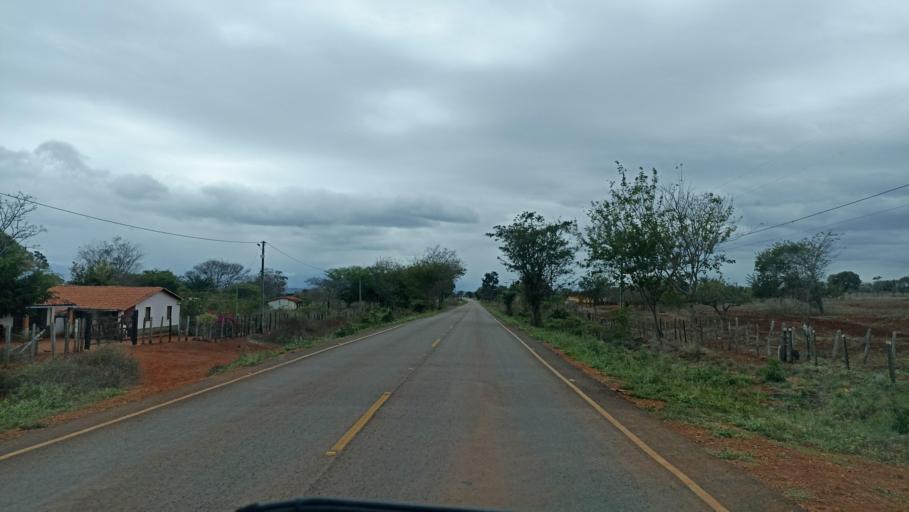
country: BR
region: Bahia
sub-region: Andarai
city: Vera Cruz
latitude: -12.9751
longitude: -41.0217
